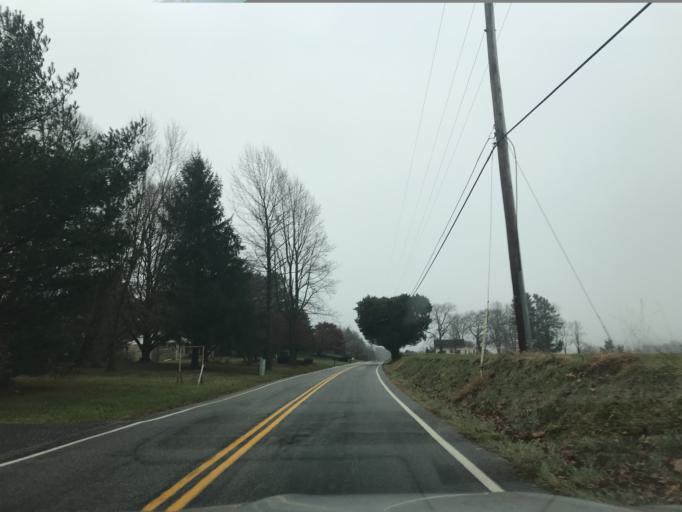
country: US
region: Maryland
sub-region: Harford County
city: South Bel Air
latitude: 39.5899
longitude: -76.2828
